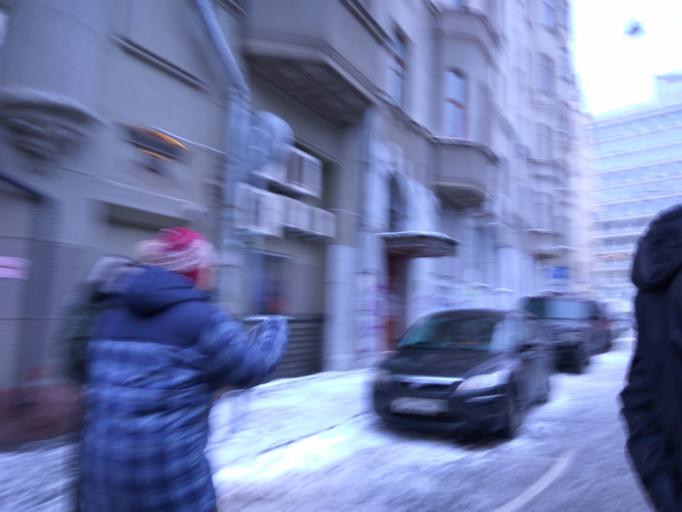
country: RU
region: Moskovskaya
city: Dorogomilovo
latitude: 55.7492
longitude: 37.5910
